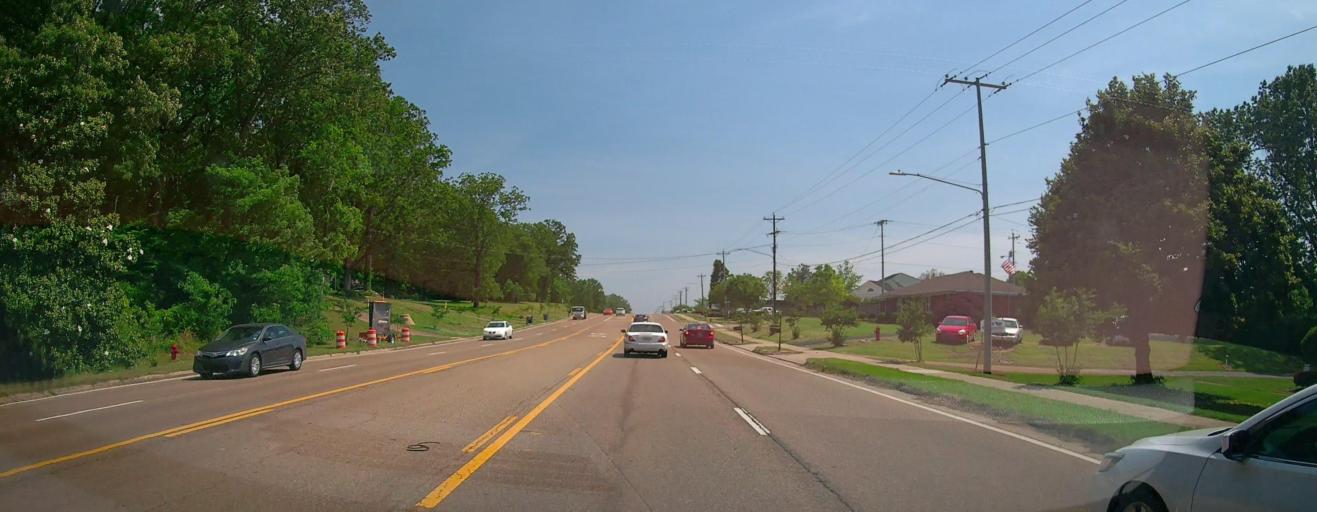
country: US
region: Mississippi
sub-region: De Soto County
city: Olive Branch
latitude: 34.9590
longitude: -89.8304
